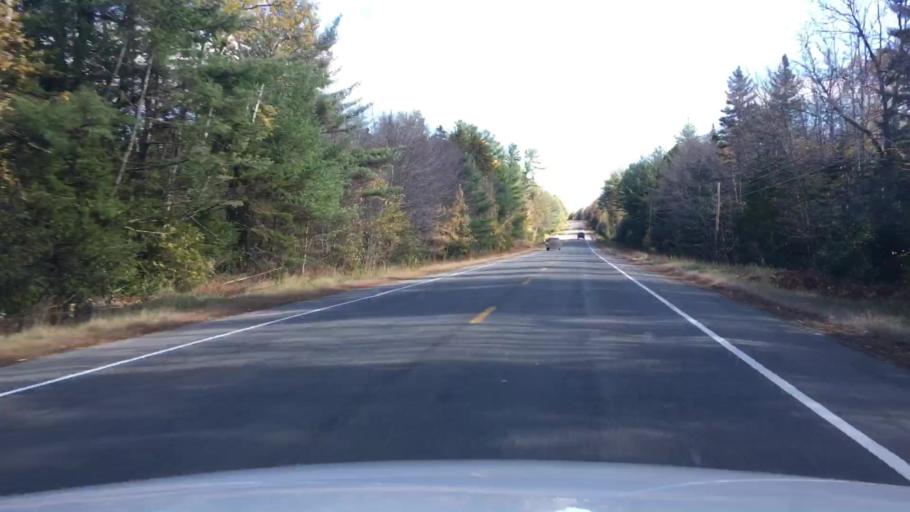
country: US
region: Maine
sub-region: Penobscot County
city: Millinocket
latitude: 45.6569
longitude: -68.6696
